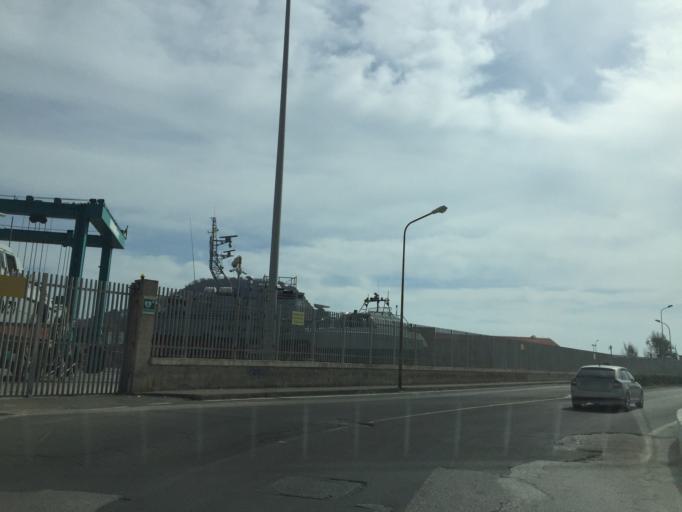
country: IT
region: Campania
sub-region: Provincia di Napoli
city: Bacoli
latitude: 40.7895
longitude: 14.0781
